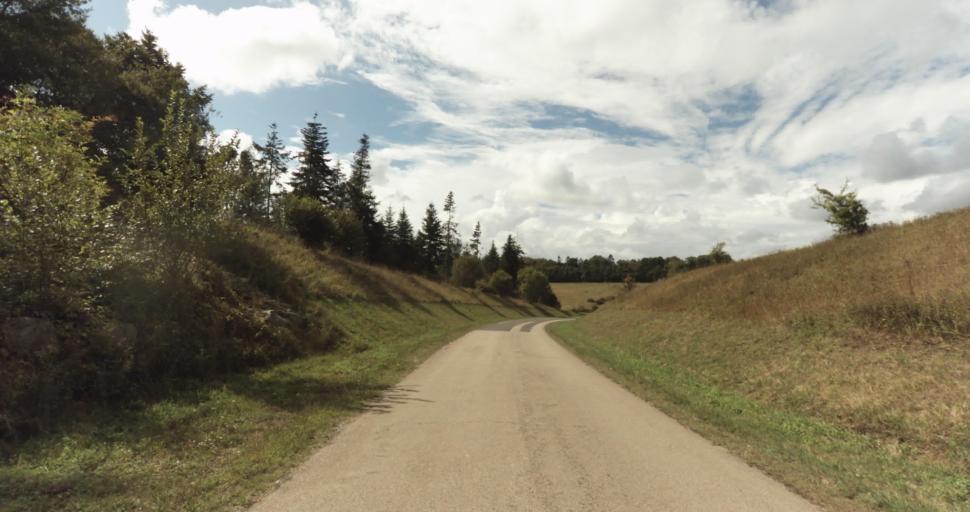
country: FR
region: Lower Normandy
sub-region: Departement de l'Orne
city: Gace
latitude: 48.7831
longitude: 0.3213
